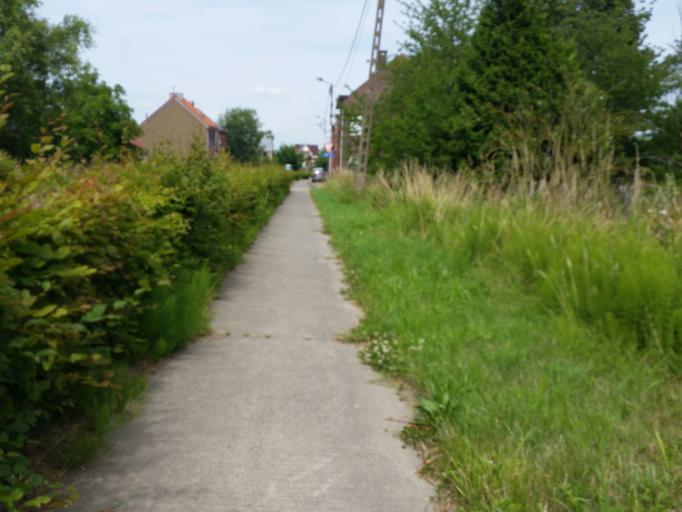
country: BE
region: Flanders
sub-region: Provincie Antwerpen
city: Rumst
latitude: 51.0448
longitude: 4.4138
